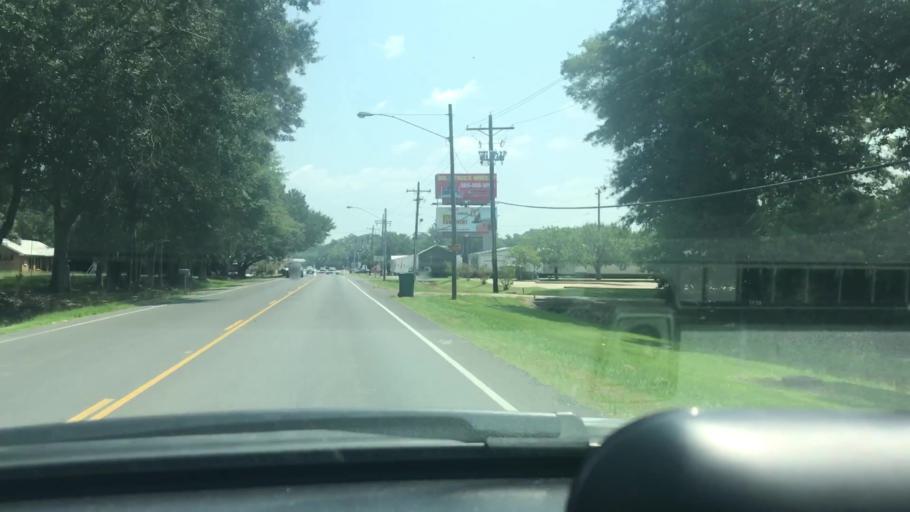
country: US
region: Louisiana
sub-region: Livingston Parish
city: Walker
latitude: 30.4877
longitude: -90.8658
